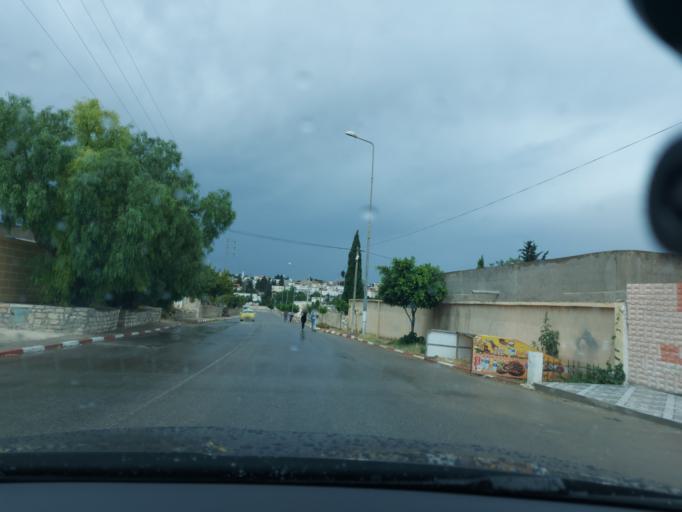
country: TN
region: Silyanah
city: Maktar
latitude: 35.8566
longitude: 9.2092
